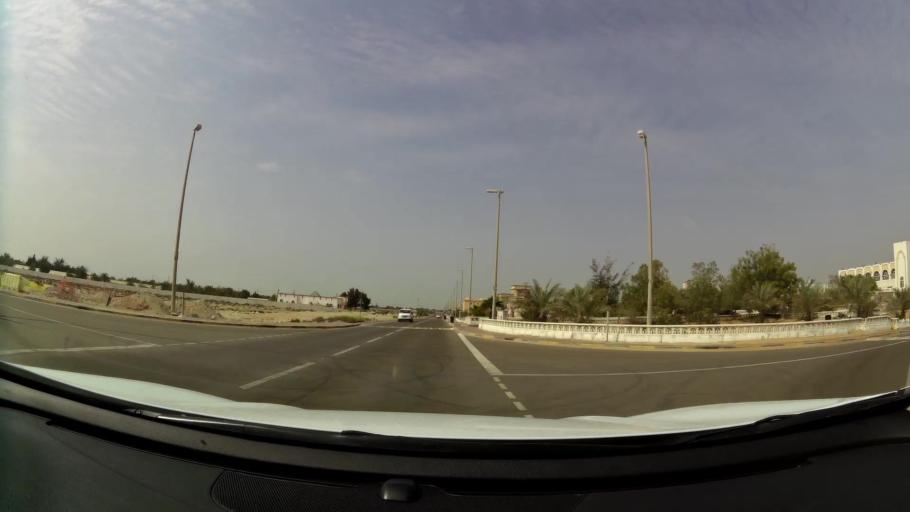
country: AE
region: Abu Dhabi
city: Abu Dhabi
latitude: 24.5394
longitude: 54.6695
